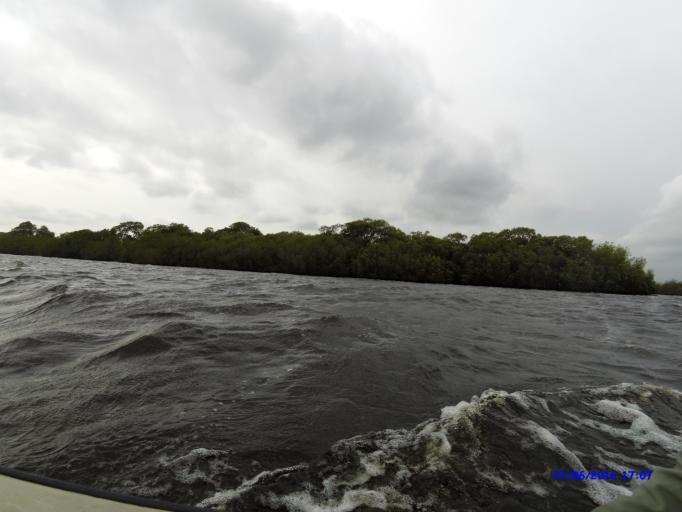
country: BJ
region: Atlantique
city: Allada
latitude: 6.6017
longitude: 1.9905
